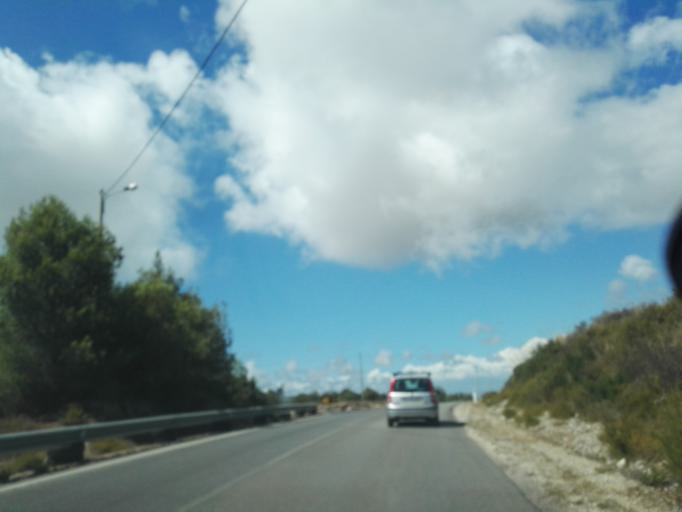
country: PT
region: Setubal
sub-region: Sesimbra
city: Sesimbra
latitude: 38.4573
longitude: -9.0938
